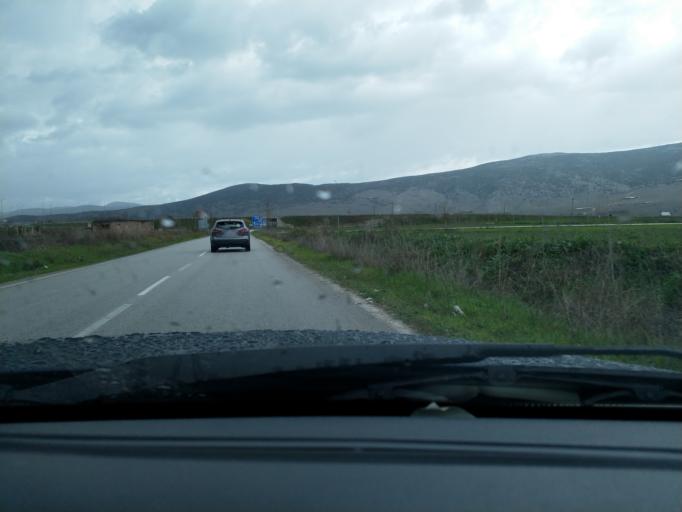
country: GR
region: Thessaly
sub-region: Trikala
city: Taxiarches
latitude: 39.5590
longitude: 21.8898
